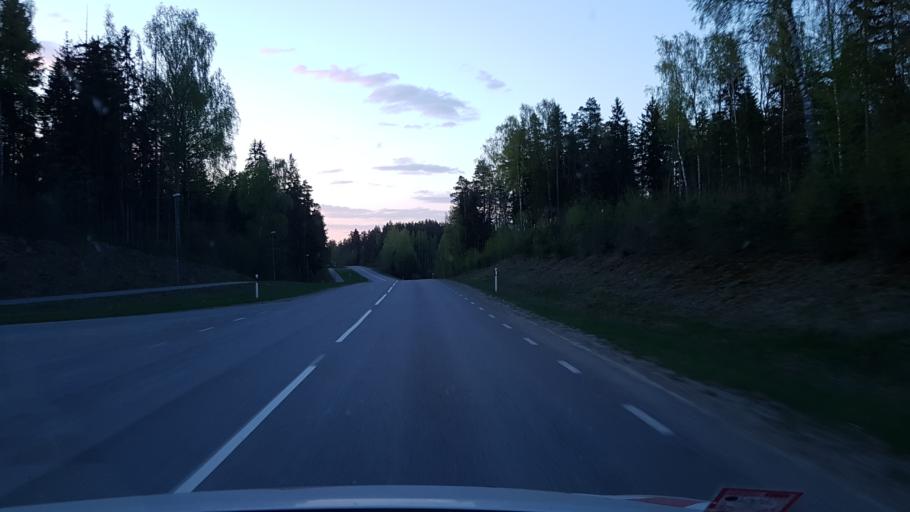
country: EE
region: Vorumaa
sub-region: Voru linn
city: Voru
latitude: 57.8007
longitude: 27.0342
